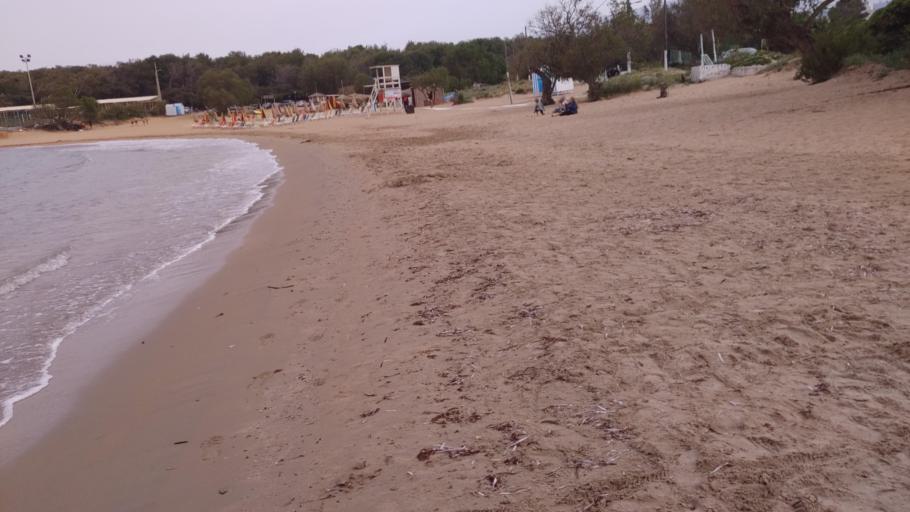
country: GR
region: Crete
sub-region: Nomos Chanias
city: Daratsos
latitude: 35.5146
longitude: 23.9777
